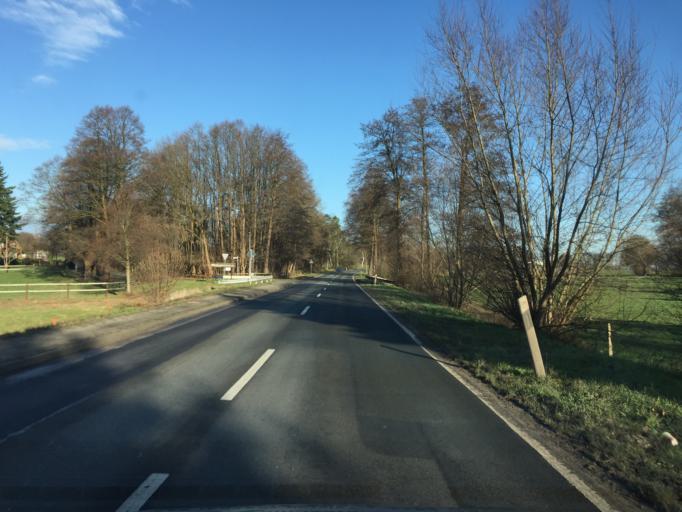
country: DE
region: Lower Saxony
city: Husum
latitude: 52.5676
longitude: 9.2546
